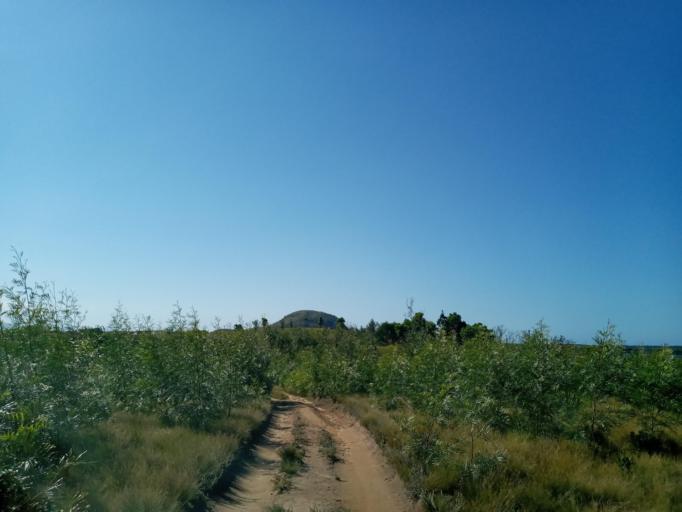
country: MG
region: Anosy
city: Fort Dauphin
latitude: -24.9119
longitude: 47.0893
